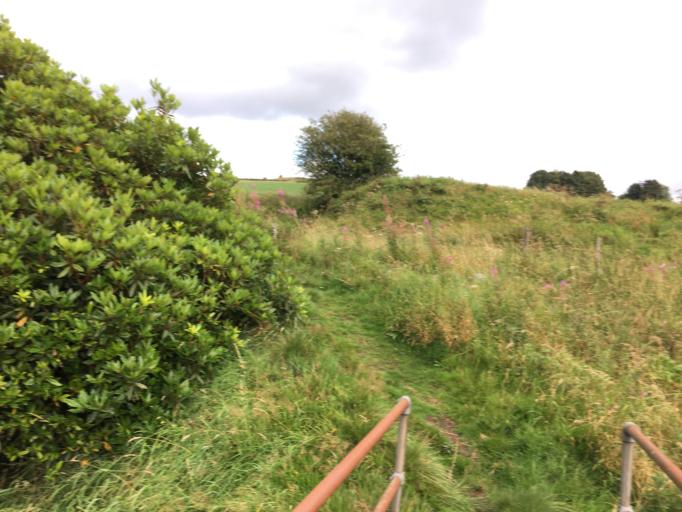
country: GB
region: England
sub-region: Borough of Oldham
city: Delph
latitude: 53.5838
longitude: -2.0429
